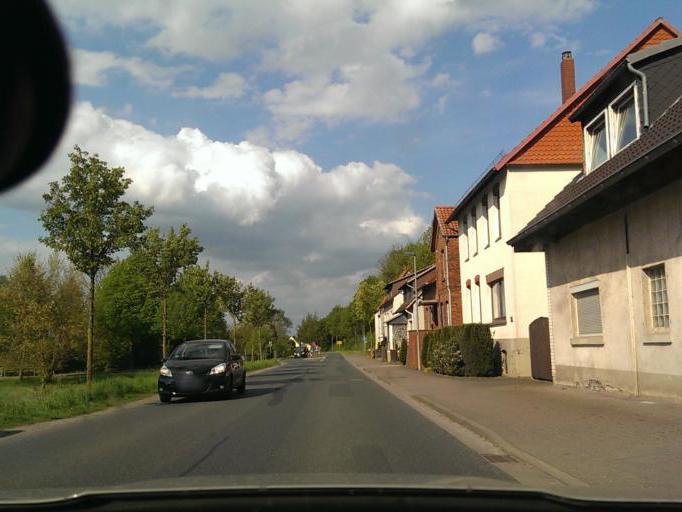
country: DE
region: Lower Saxony
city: Eime
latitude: 52.0683
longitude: 9.7094
